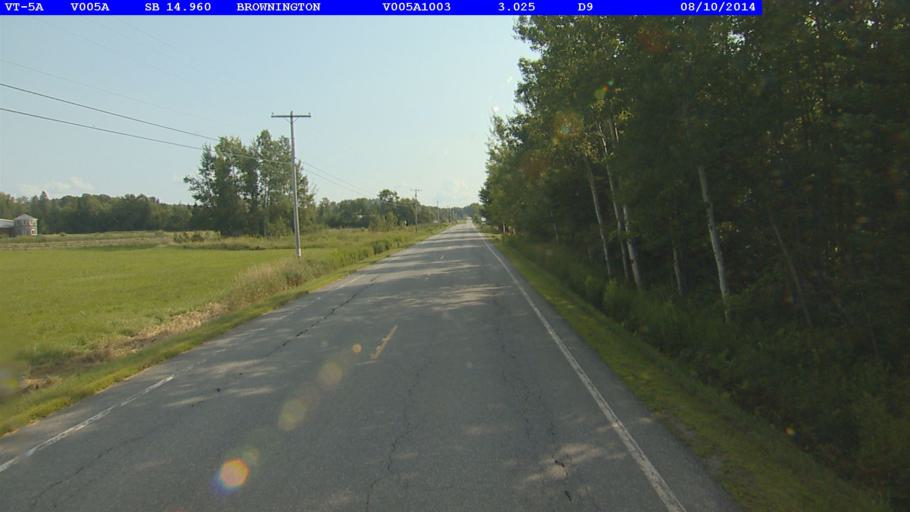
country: US
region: Vermont
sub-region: Orleans County
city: Newport
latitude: 44.8256
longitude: -72.0707
